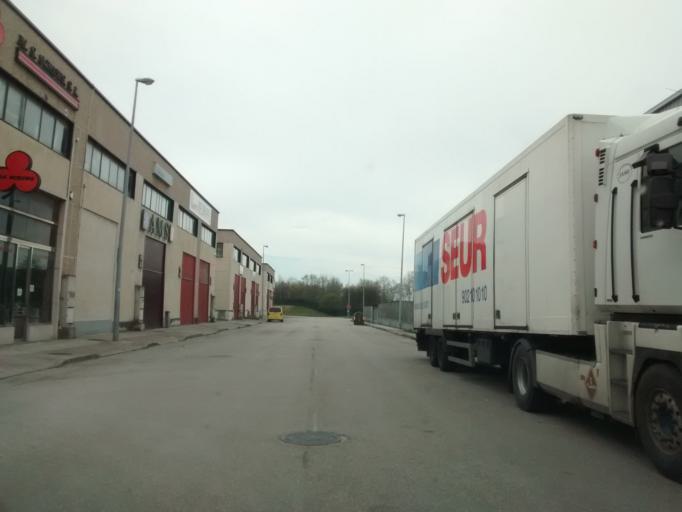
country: ES
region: Cantabria
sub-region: Provincia de Cantabria
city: El Astillero
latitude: 43.4262
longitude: -3.8428
